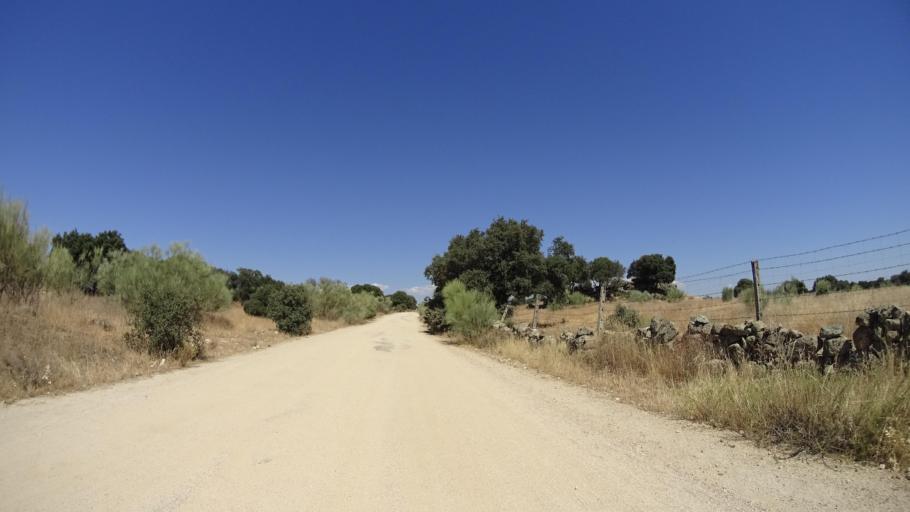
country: ES
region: Madrid
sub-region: Provincia de Madrid
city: Colmenarejo
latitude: 40.5330
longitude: -4.0108
